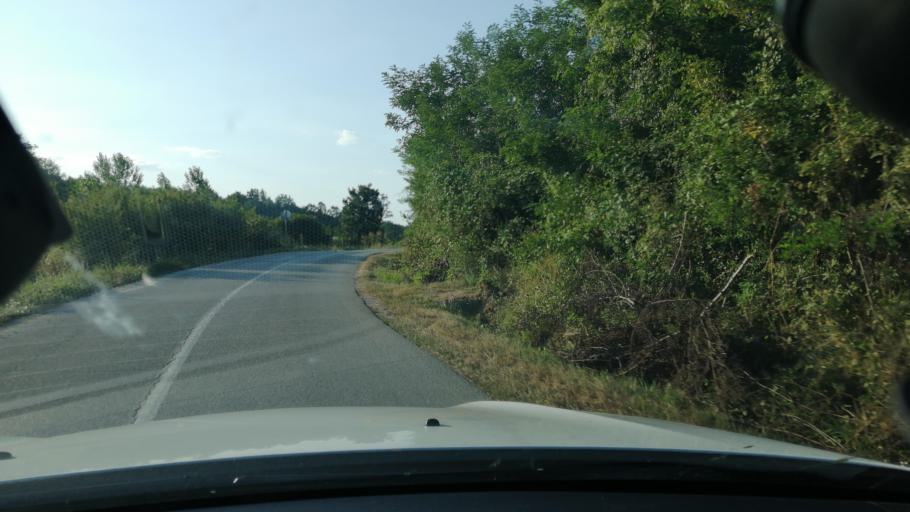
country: RS
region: Central Serbia
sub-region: Moravicki Okrug
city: Cacak
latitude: 43.8002
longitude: 20.2550
